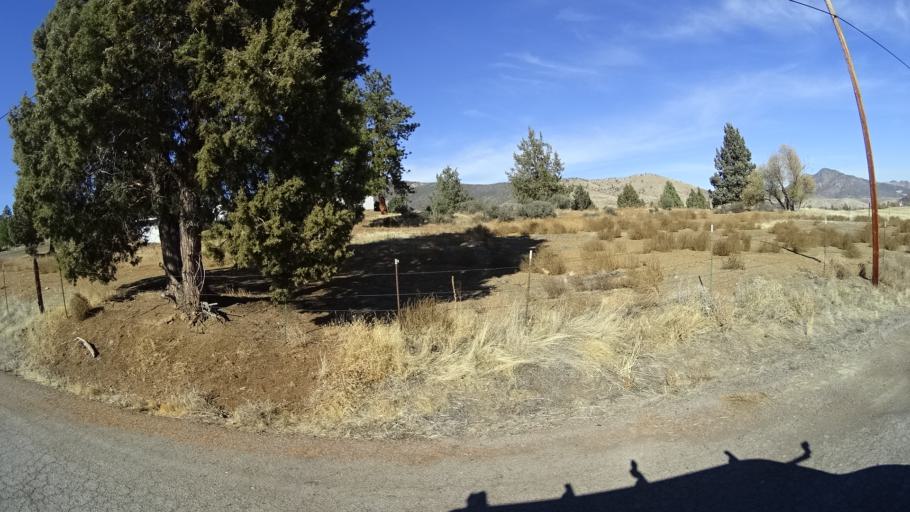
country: US
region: California
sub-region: Siskiyou County
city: Yreka
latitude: 41.7602
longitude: -122.6285
